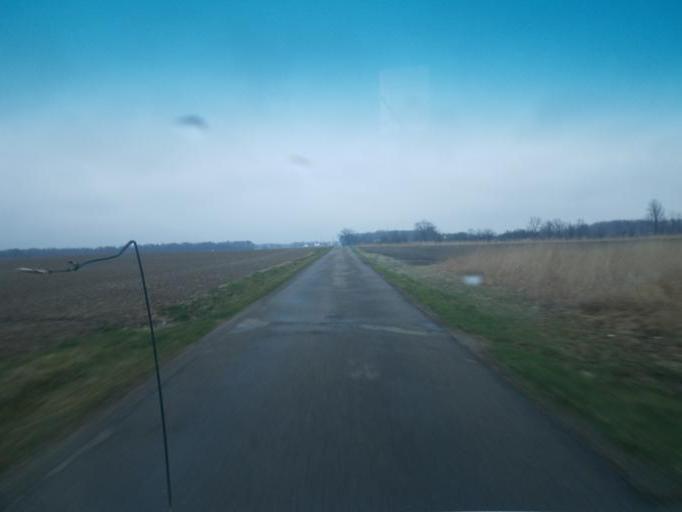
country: US
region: Ohio
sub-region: Defiance County
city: Hicksville
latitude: 41.3392
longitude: -84.7526
